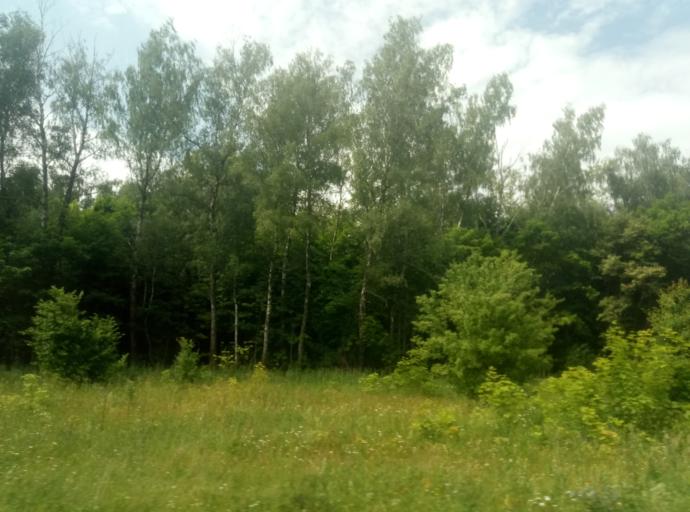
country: RU
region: Tula
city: Bogoroditsk
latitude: 53.8245
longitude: 38.1188
